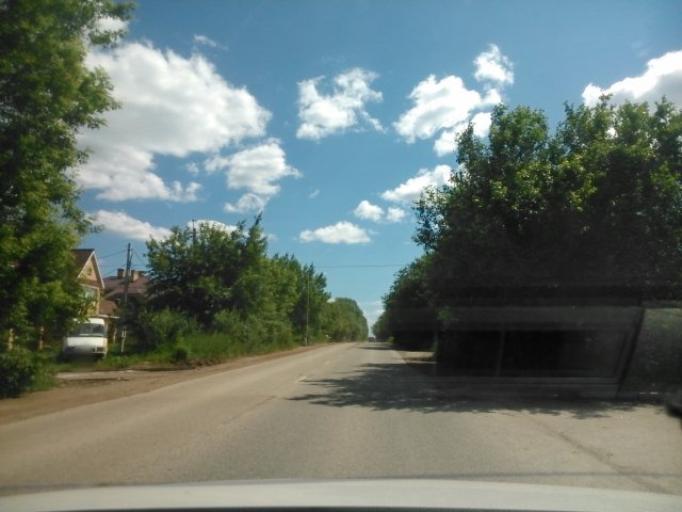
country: RU
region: Perm
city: Perm
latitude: 58.0036
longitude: 56.3289
